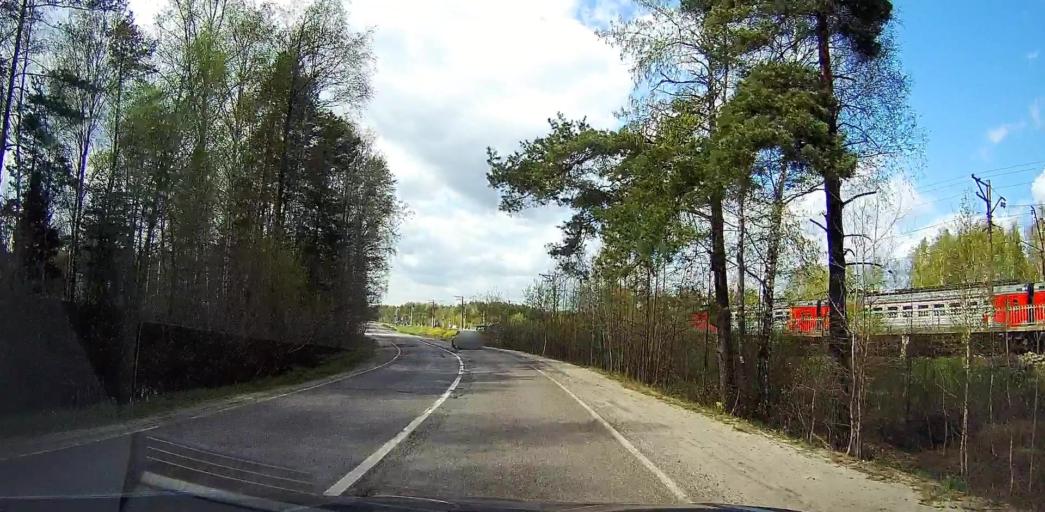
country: RU
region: Moskovskaya
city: Davydovo
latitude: 55.5720
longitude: 38.8220
